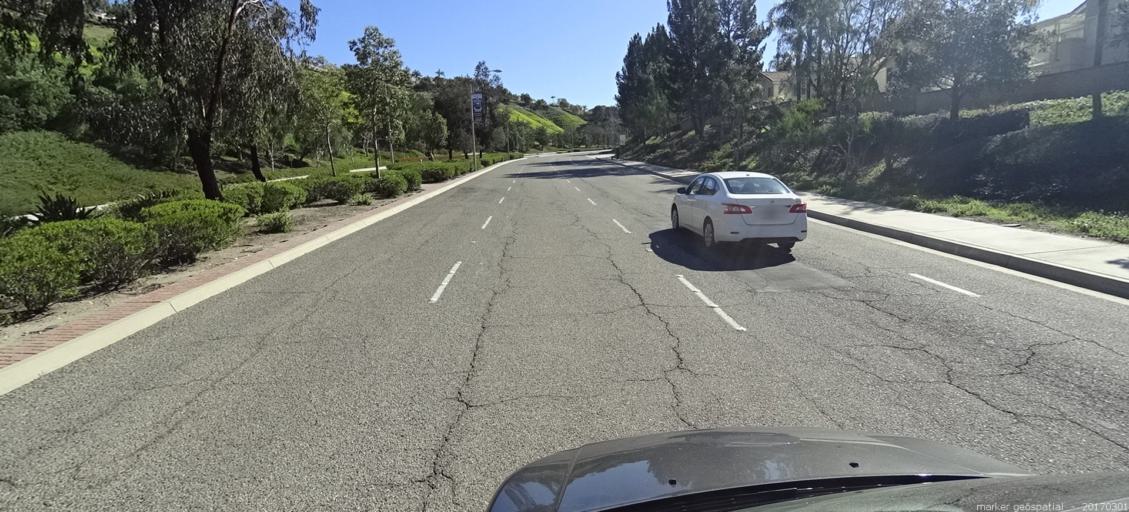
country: US
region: California
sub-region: Orange County
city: Yorba Linda
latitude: 33.8615
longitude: -117.7333
